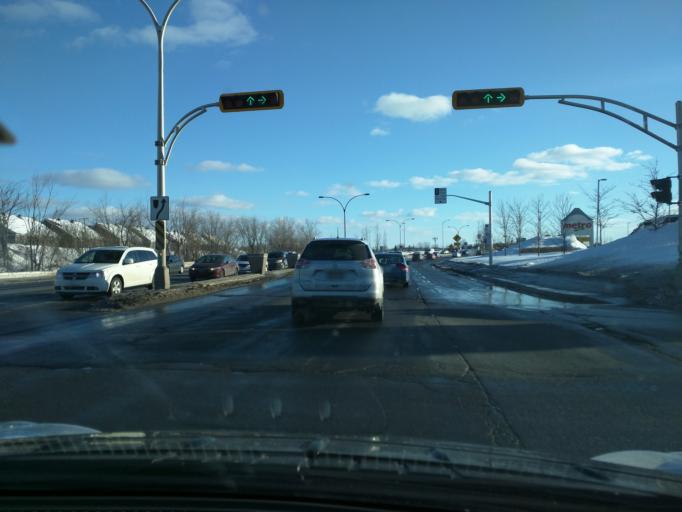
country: CA
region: Quebec
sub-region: Laurentides
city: Rosemere
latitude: 45.5893
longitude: -73.7862
